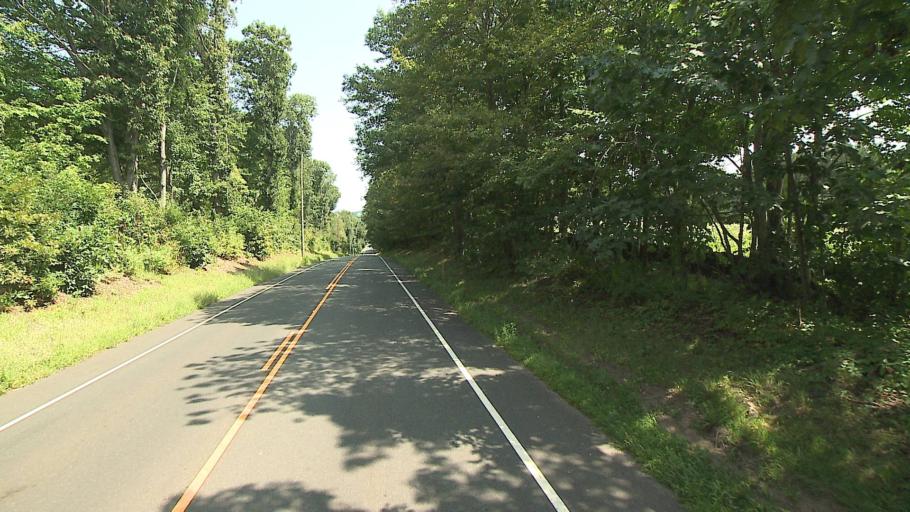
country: US
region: Connecticut
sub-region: Fairfield County
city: Shelton
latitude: 41.3347
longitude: -73.1770
